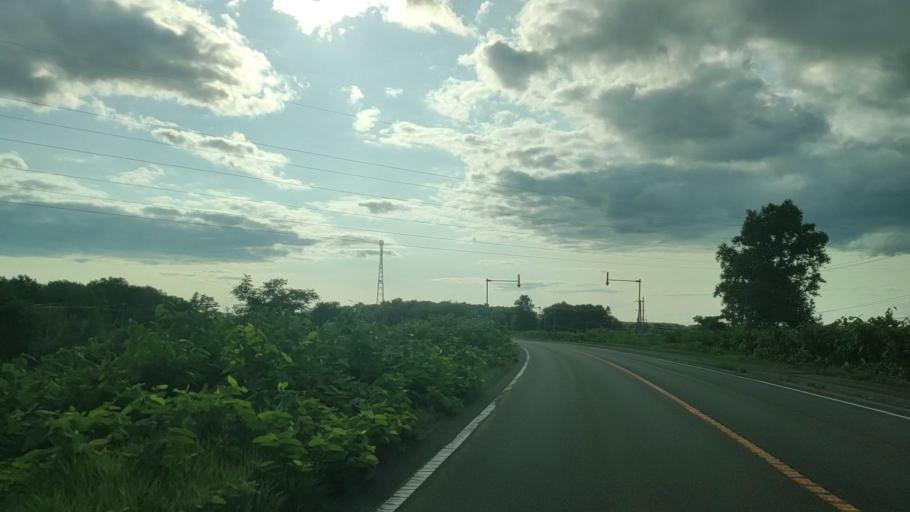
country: JP
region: Hokkaido
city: Makubetsu
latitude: 44.8998
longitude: 141.9374
